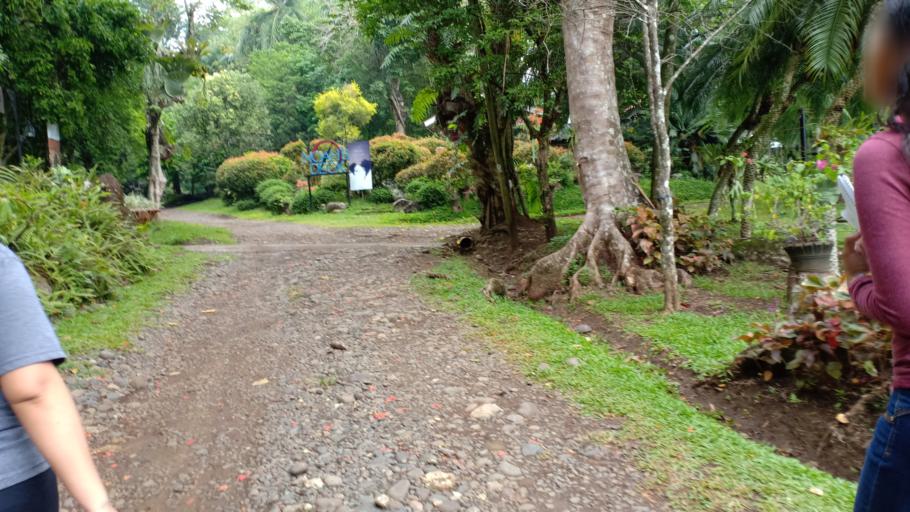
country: PH
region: Davao
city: Malagos
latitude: 7.1909
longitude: 125.4274
